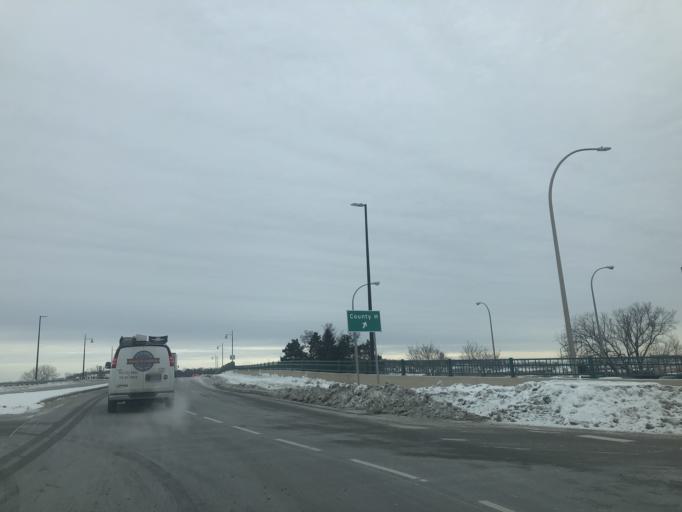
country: US
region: Minnesota
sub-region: Ramsey County
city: Mounds View
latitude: 45.0954
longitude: -93.1900
